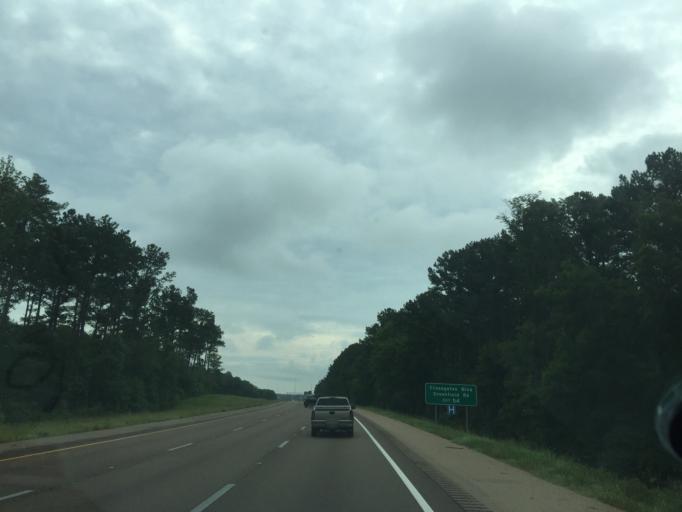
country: US
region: Mississippi
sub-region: Rankin County
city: Brandon
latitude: 32.2742
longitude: -90.0527
